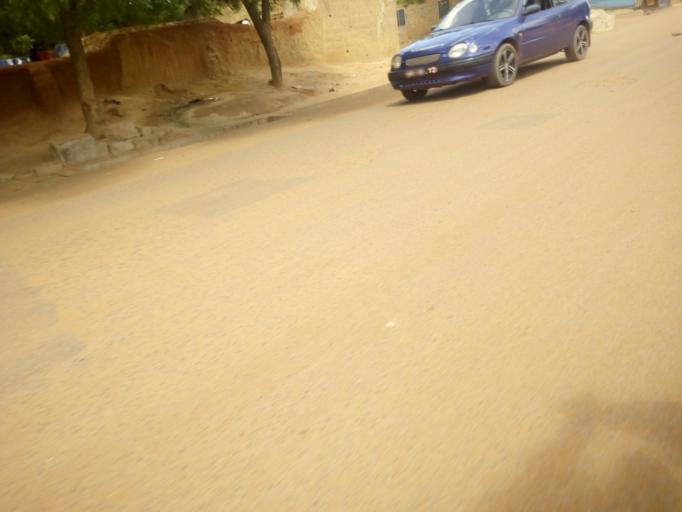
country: ML
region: Segou
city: Segou
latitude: 13.4319
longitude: -6.2634
